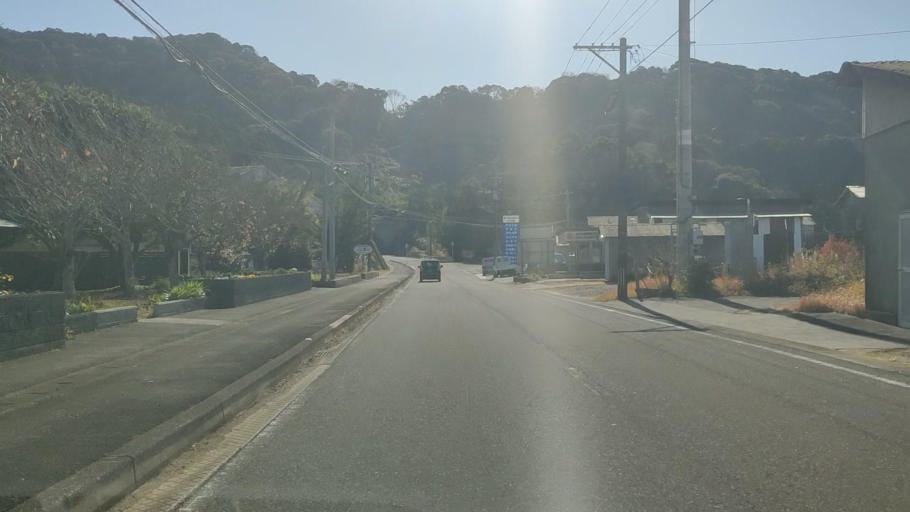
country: JP
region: Oita
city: Saiki
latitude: 32.7997
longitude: 131.9001
